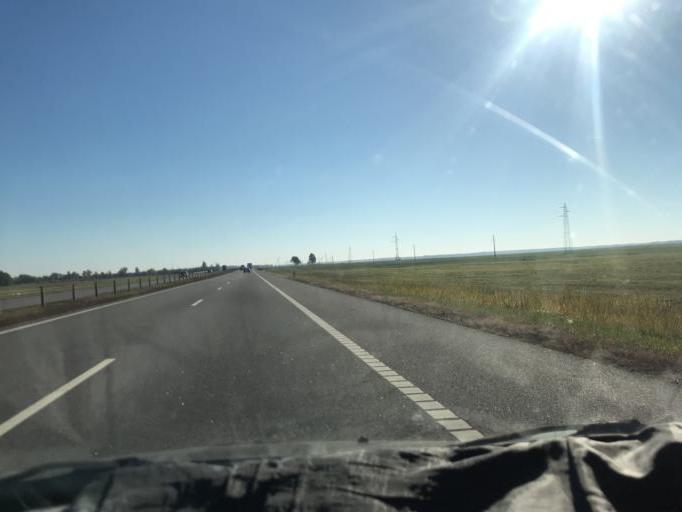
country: BY
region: Mogilev
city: Yalizava
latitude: 53.2385
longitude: 28.9628
